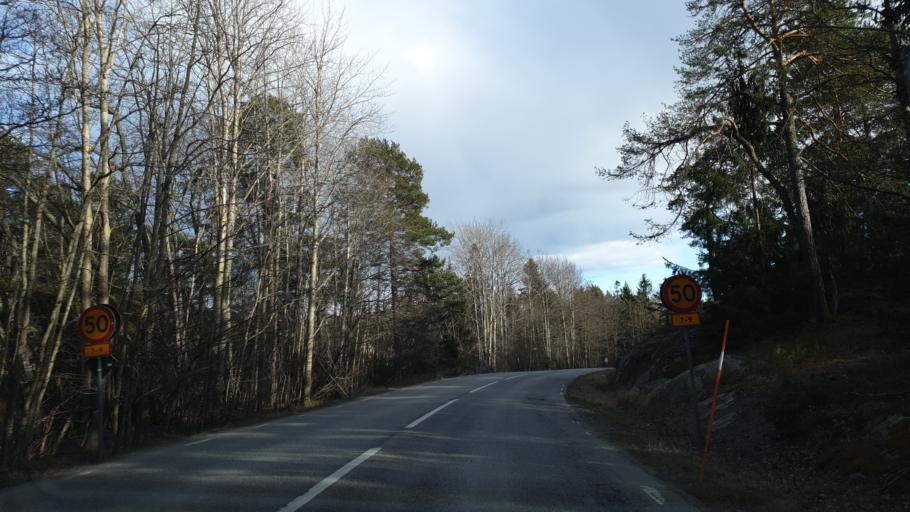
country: SE
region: Stockholm
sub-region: Varmdo Kommun
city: Holo
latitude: 59.3289
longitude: 18.7224
